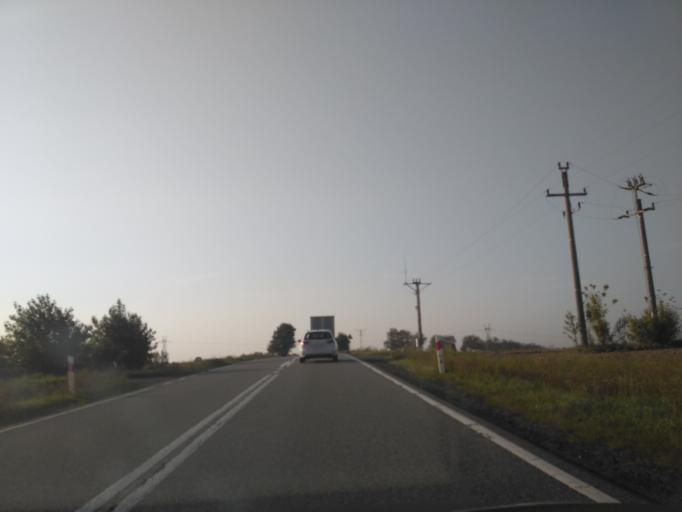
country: PL
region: Lublin Voivodeship
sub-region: Powiat krasnicki
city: Szastarka
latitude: 50.8188
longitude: 22.3168
